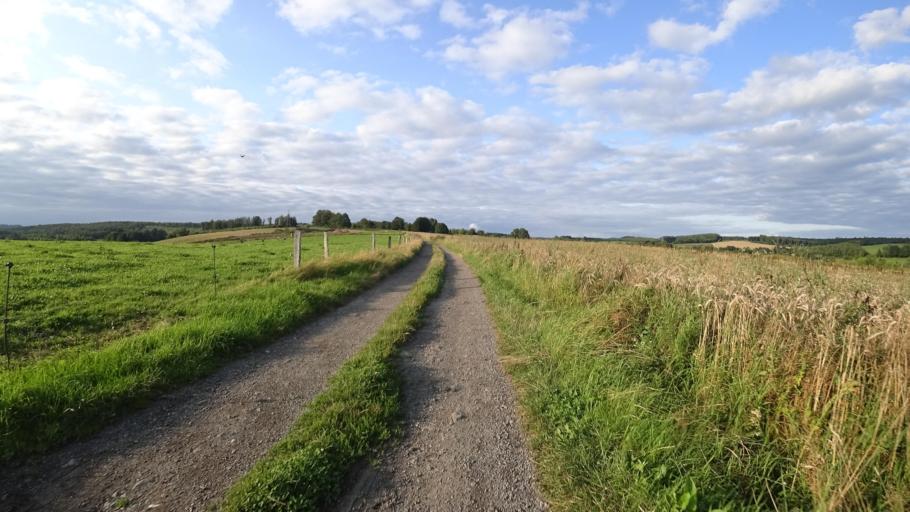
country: BE
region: Wallonia
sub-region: Province du Luxembourg
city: Neufchateau
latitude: 49.8599
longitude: 5.3697
